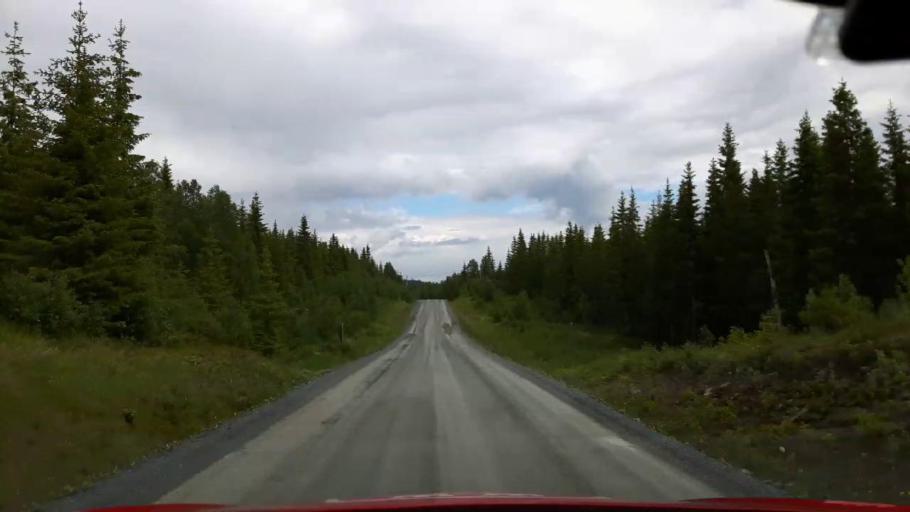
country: NO
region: Nord-Trondelag
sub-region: Lierne
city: Sandvika
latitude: 64.1444
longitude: 13.9251
